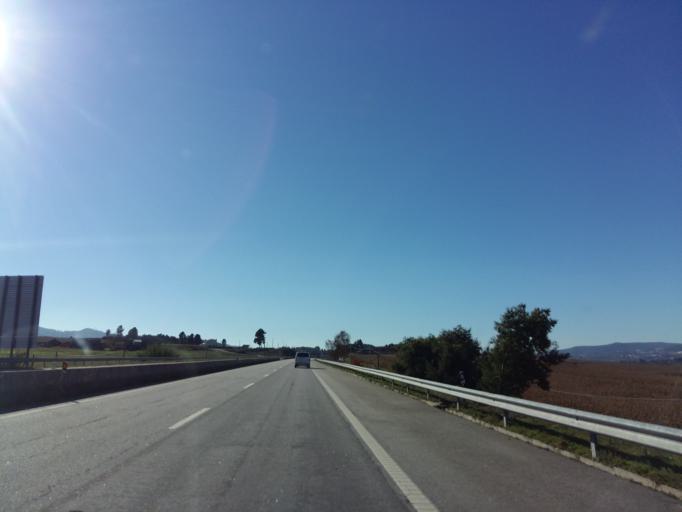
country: PT
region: Castelo Branco
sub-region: Covilha
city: Teixoso
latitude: 40.2547
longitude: -7.4483
